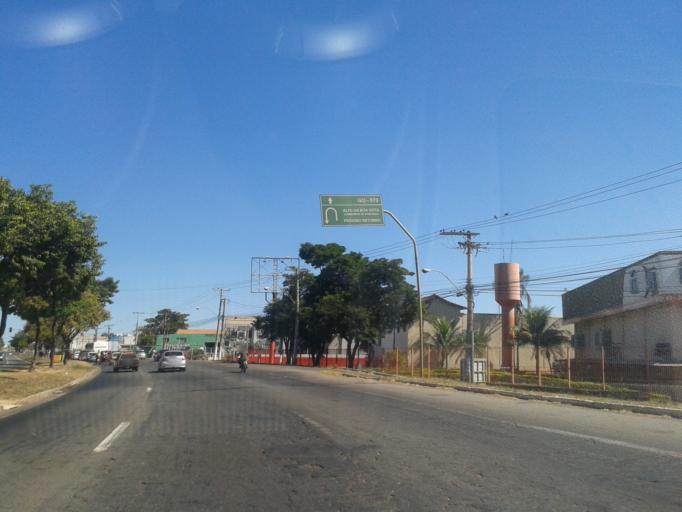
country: BR
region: Goias
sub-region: Goiania
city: Goiania
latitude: -16.6420
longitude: -49.3046
